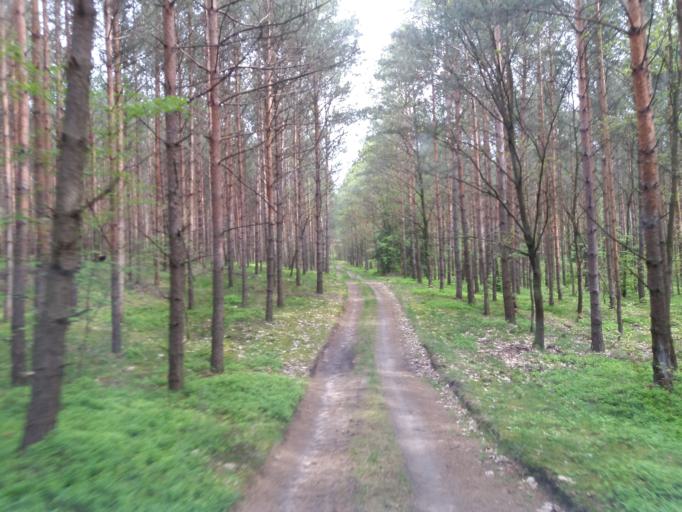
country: PL
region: West Pomeranian Voivodeship
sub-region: Powiat choszczenski
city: Bierzwnik
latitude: 52.9851
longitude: 15.6158
